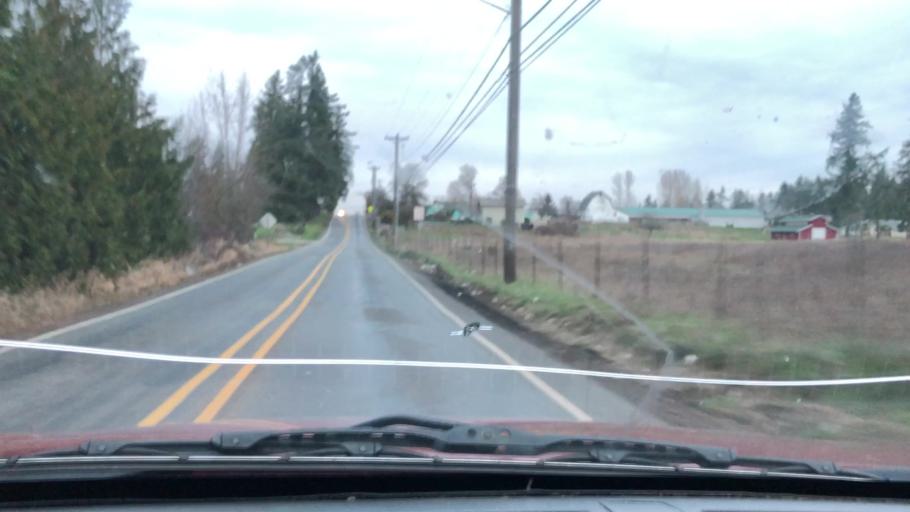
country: US
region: Washington
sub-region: Pierce County
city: Elk Plain
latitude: 47.0683
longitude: -122.4004
